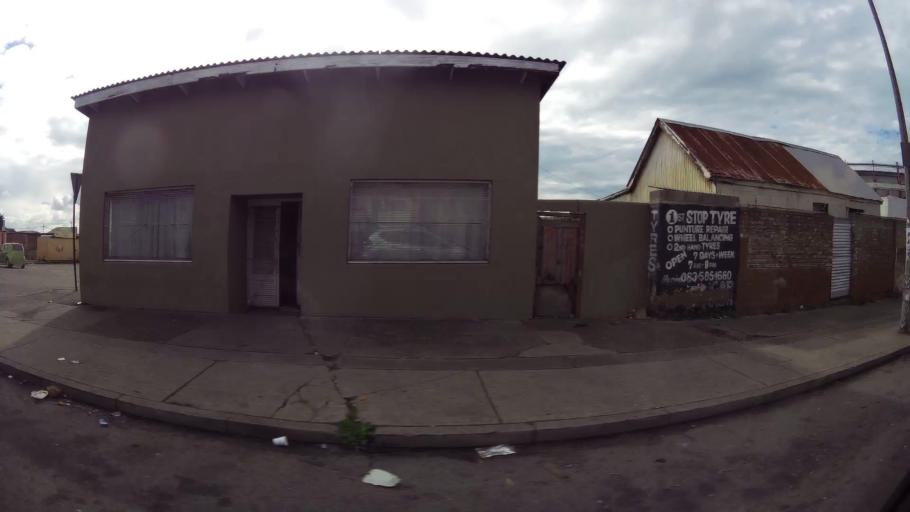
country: ZA
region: Eastern Cape
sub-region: Nelson Mandela Bay Metropolitan Municipality
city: Port Elizabeth
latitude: -33.9360
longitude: 25.5809
